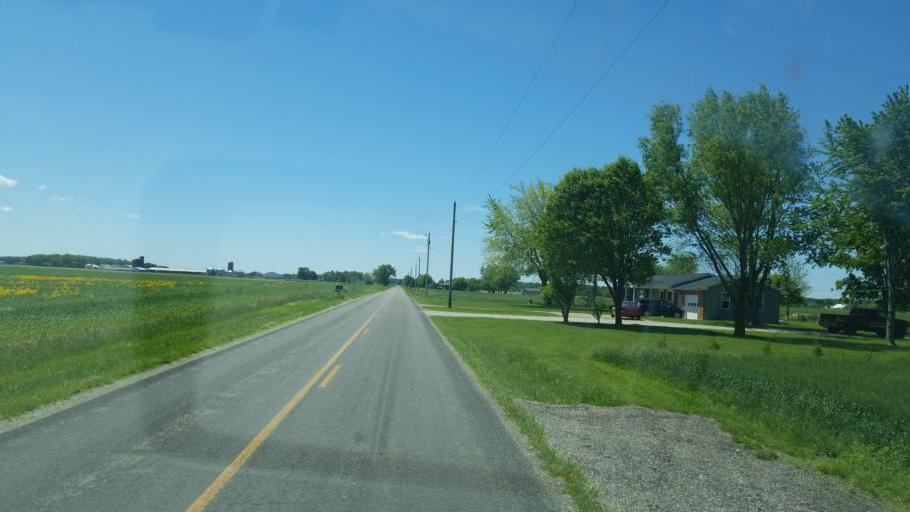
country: US
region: Ohio
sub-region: Shelby County
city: Fort Loramie
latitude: 40.3684
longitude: -84.2975
